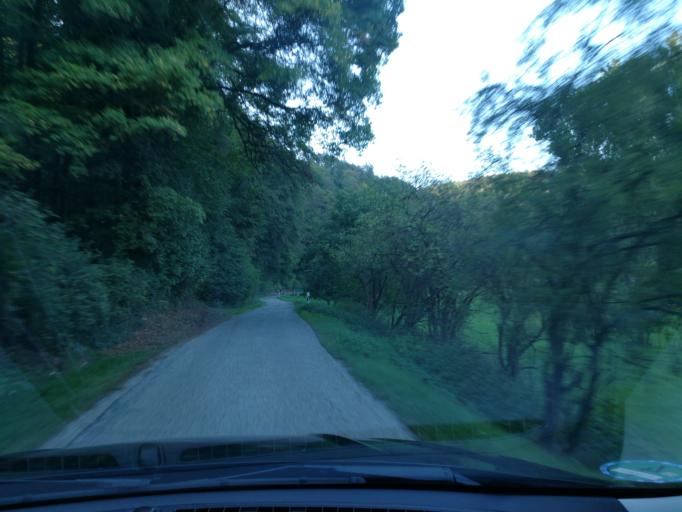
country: DE
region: Bavaria
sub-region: Lower Bavaria
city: Essing
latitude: 48.8961
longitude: 11.8167
